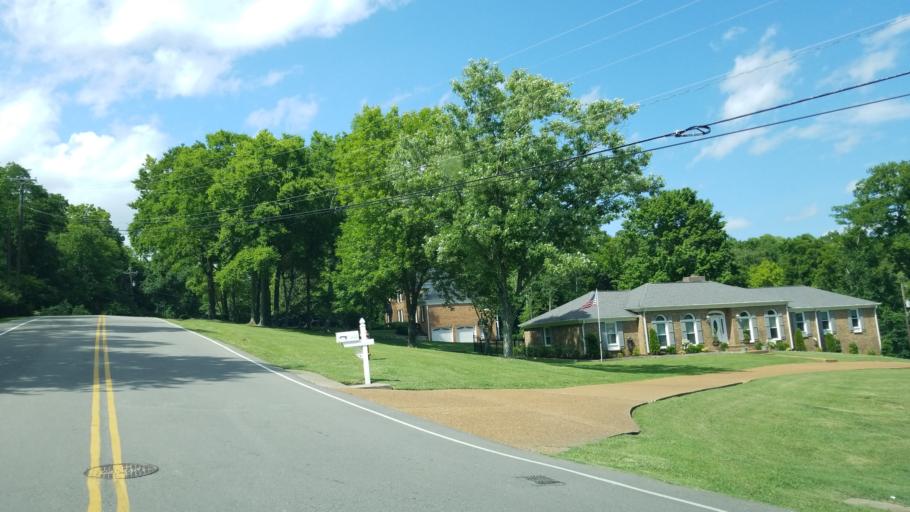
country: US
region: Tennessee
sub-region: Williamson County
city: Brentwood
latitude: 36.0459
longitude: -86.7831
